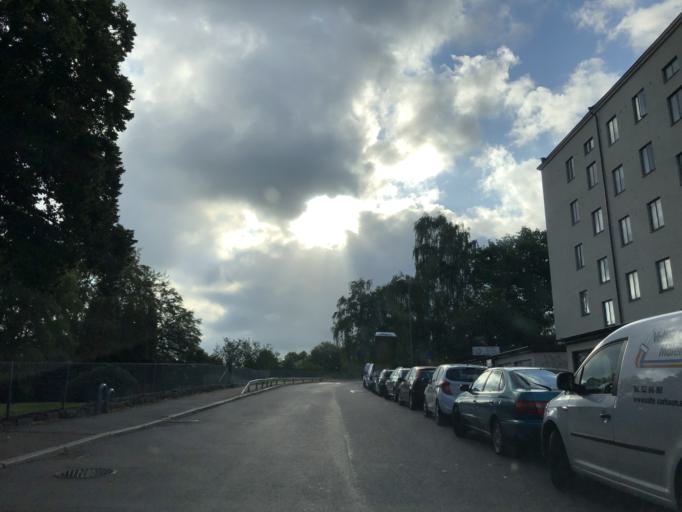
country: SE
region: Vaestra Goetaland
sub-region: Goteborg
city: Goeteborg
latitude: 57.7135
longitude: 12.0132
